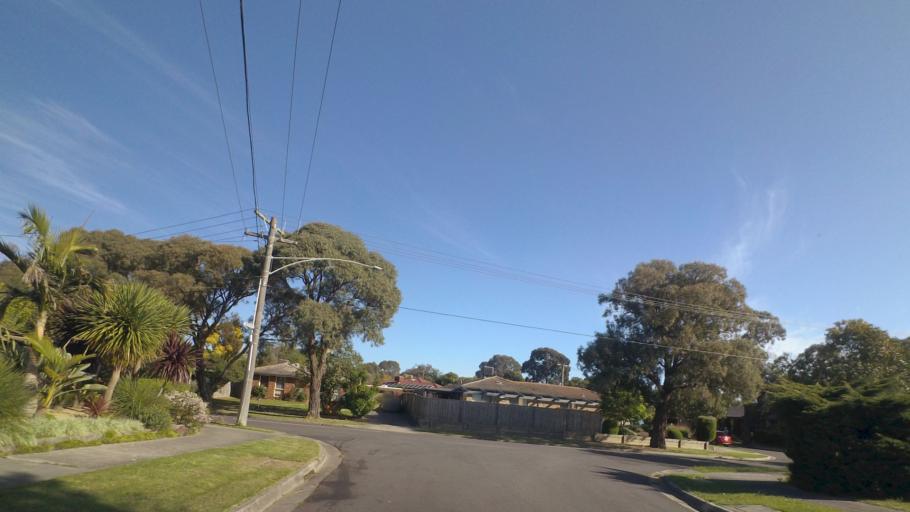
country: AU
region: Victoria
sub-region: Maroondah
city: Heathmont
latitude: -37.8388
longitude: 145.2533
